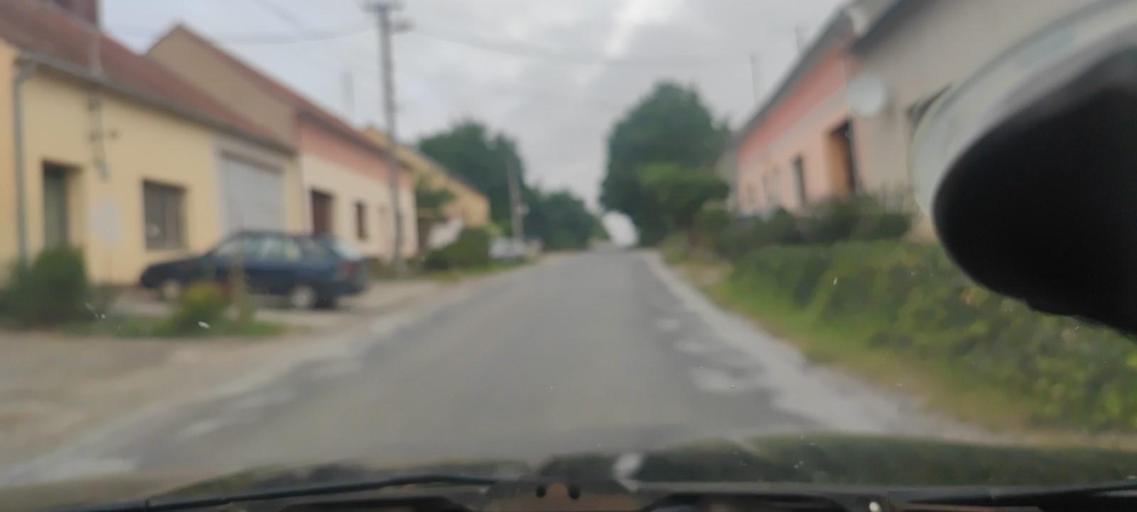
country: CZ
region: South Moravian
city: Hosteradice
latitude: 48.9516
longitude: 16.2421
